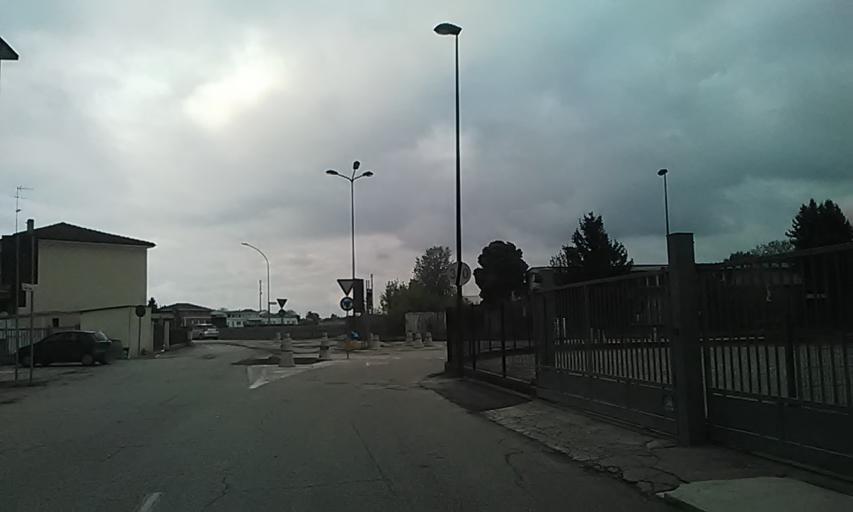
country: IT
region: Piedmont
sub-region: Provincia di Alessandria
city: Casale Monferrato
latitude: 45.1465
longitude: 8.4417
